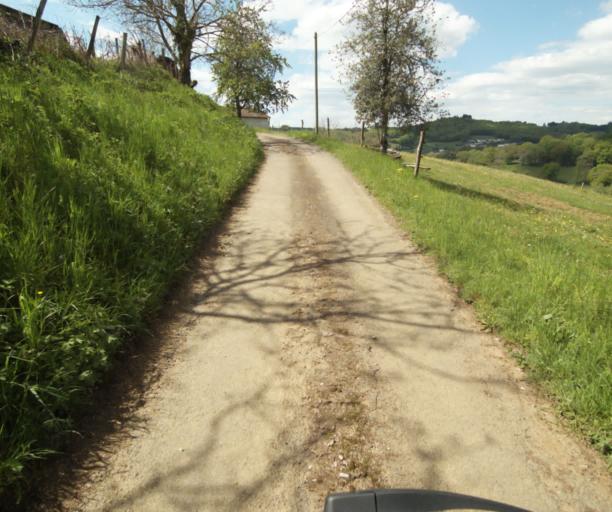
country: FR
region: Limousin
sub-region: Departement de la Correze
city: Tulle
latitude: 45.2898
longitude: 1.7763
